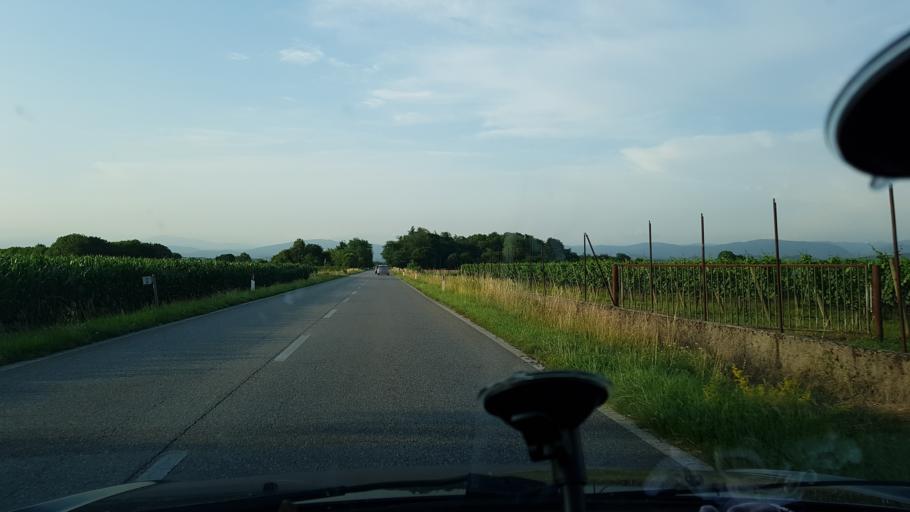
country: IT
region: Friuli Venezia Giulia
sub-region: Provincia di Gorizia
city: Gradisca d'Isonzo
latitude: 45.9092
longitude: 13.4975
